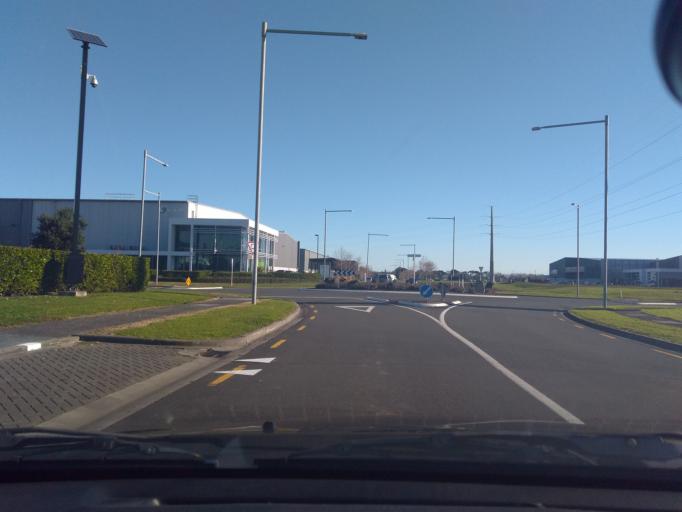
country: NZ
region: Auckland
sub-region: Auckland
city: Tamaki
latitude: -36.9297
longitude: 174.8745
